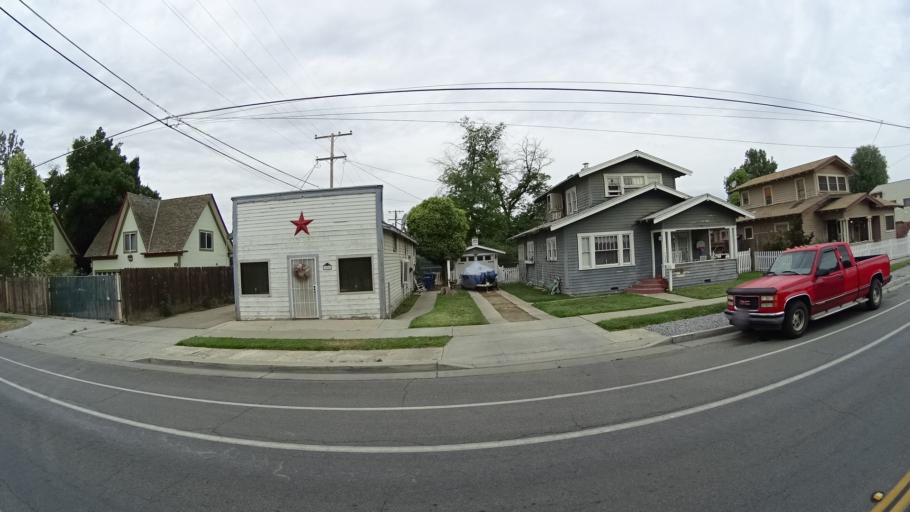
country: US
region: California
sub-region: Kings County
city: Hanford
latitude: 36.3354
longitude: -119.6493
